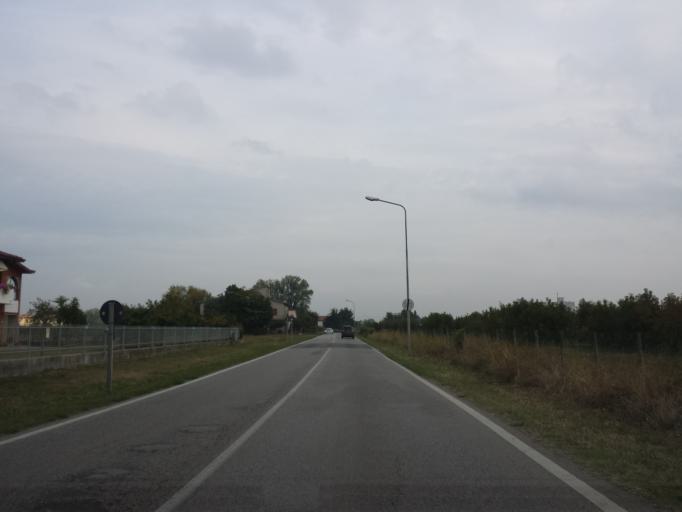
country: IT
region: Veneto
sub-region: Provincia di Verona
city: San Gregorio
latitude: 45.3399
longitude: 11.2876
